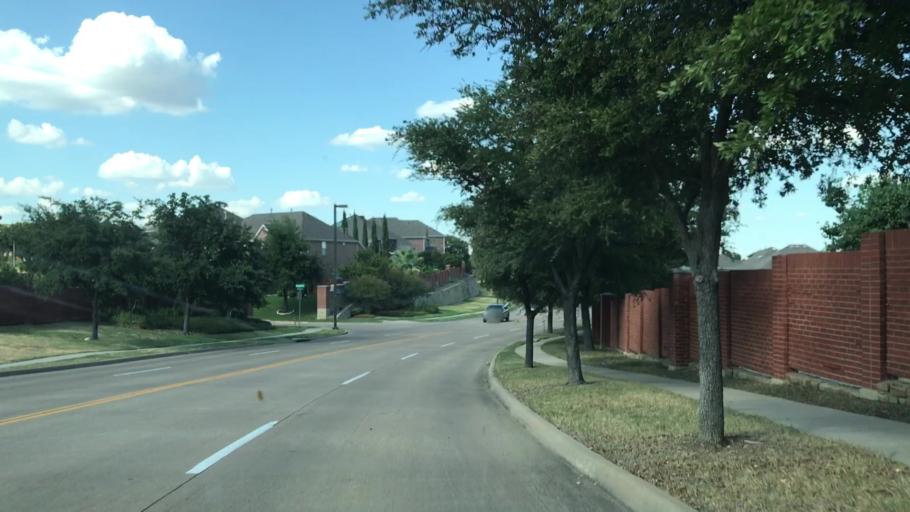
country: US
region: Texas
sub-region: Dallas County
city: Coppell
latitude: 32.9281
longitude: -96.9658
